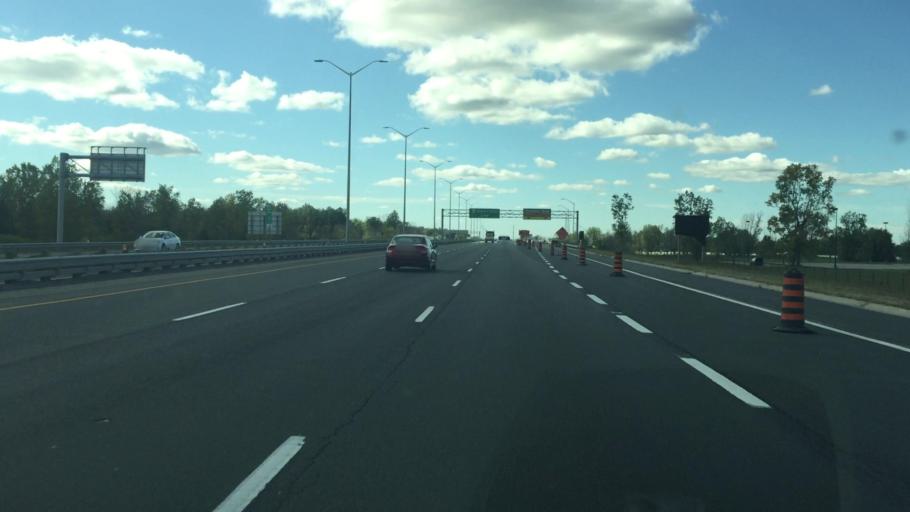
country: CA
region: Ontario
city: Fort Erie
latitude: 42.9103
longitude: -78.9301
